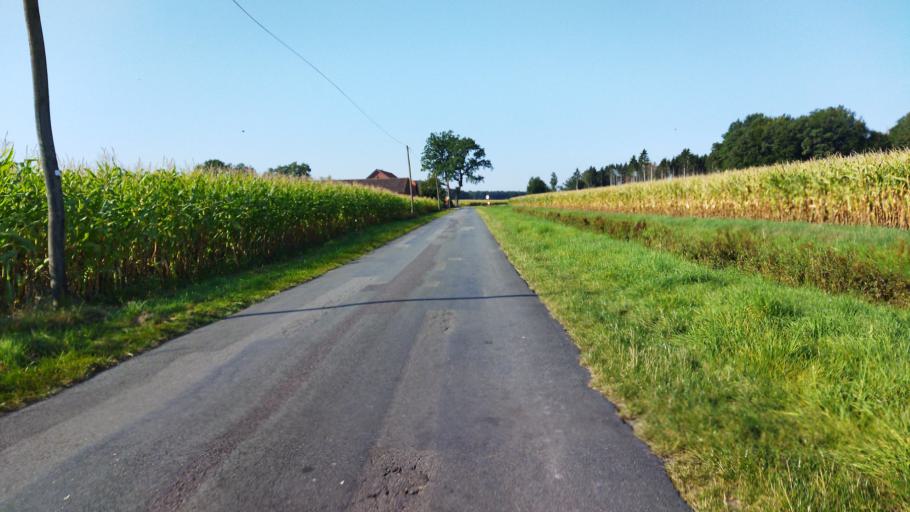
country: DE
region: Lower Saxony
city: Bad Laer
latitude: 52.1190
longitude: 8.0532
